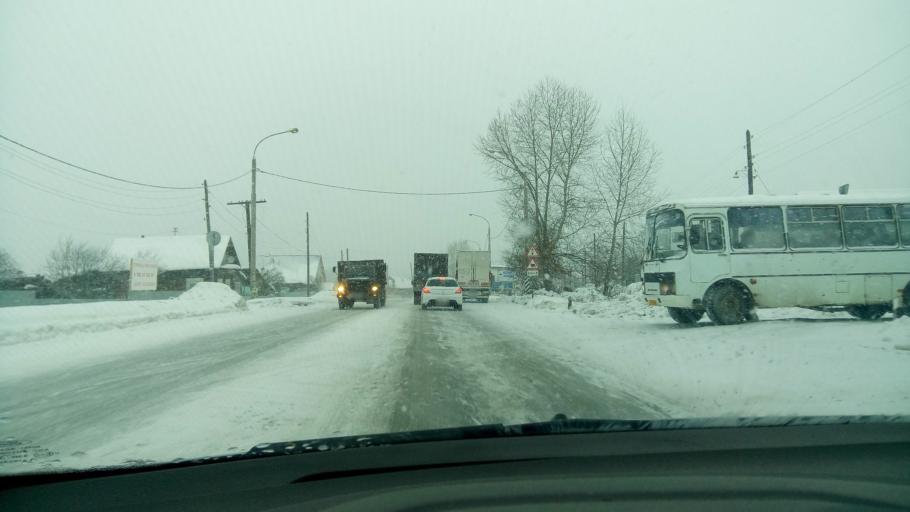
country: RU
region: Sverdlovsk
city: Beloyarskiy
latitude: 56.7638
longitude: 61.4204
